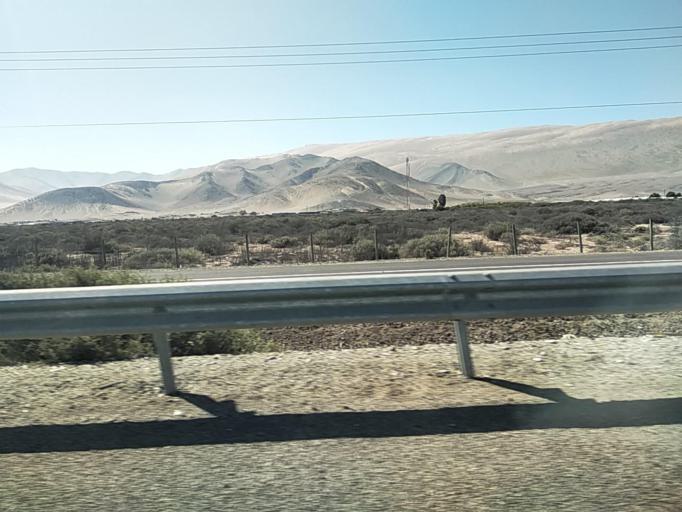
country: CL
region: Atacama
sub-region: Provincia de Copiapo
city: Copiapo
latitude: -27.2947
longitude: -70.4711
